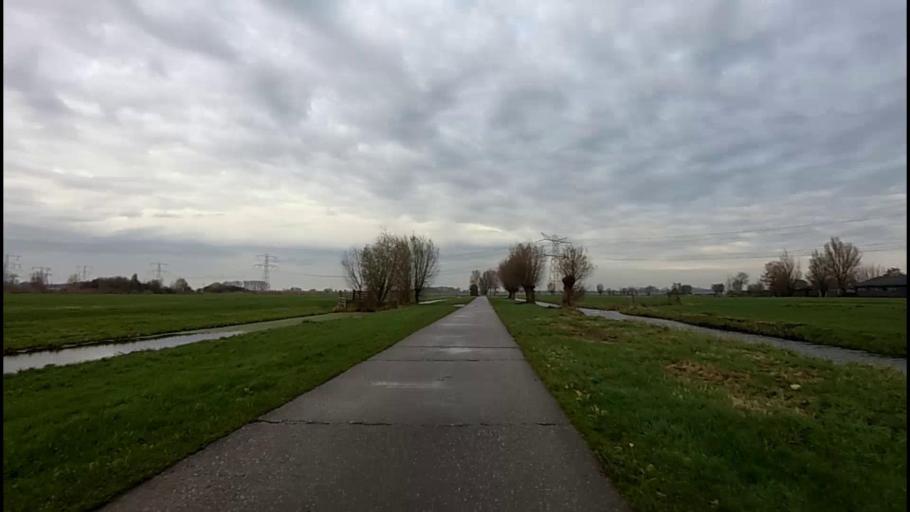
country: NL
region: South Holland
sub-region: Molenwaard
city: Nieuw-Lekkerland
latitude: 51.9036
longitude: 4.6579
